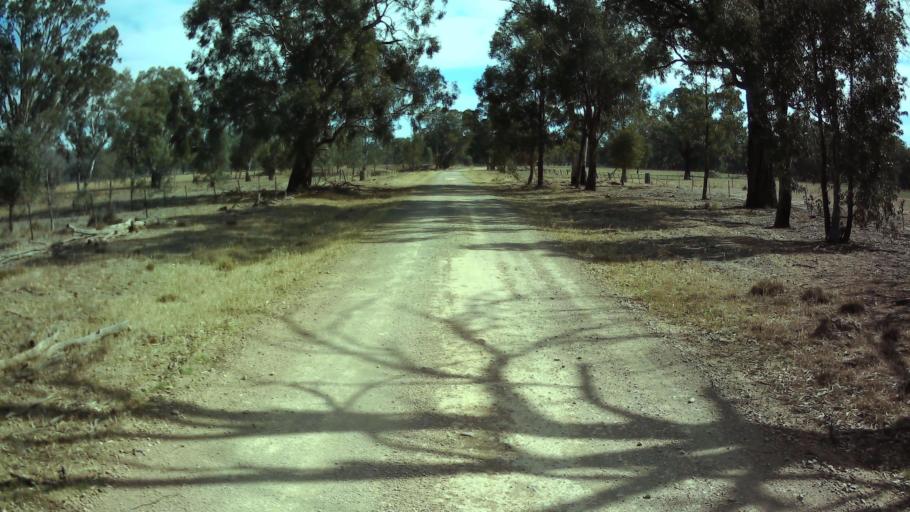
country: AU
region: New South Wales
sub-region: Weddin
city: Grenfell
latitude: -33.6930
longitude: 148.3036
